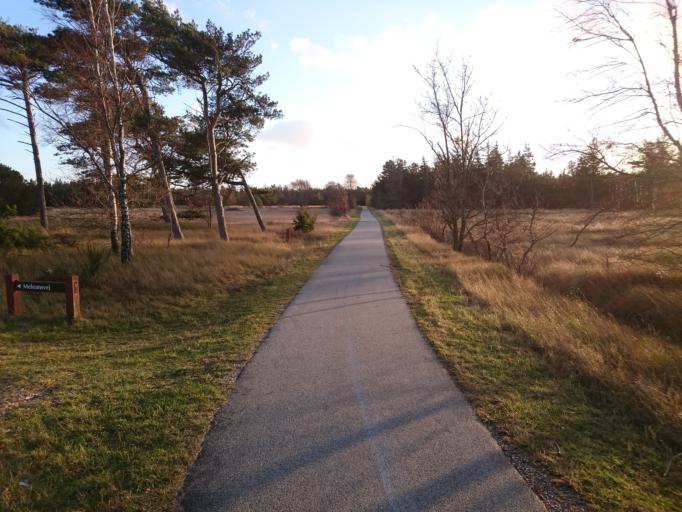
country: DK
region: North Denmark
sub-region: Frederikshavn Kommune
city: Skagen
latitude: 57.7082
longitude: 10.5236
